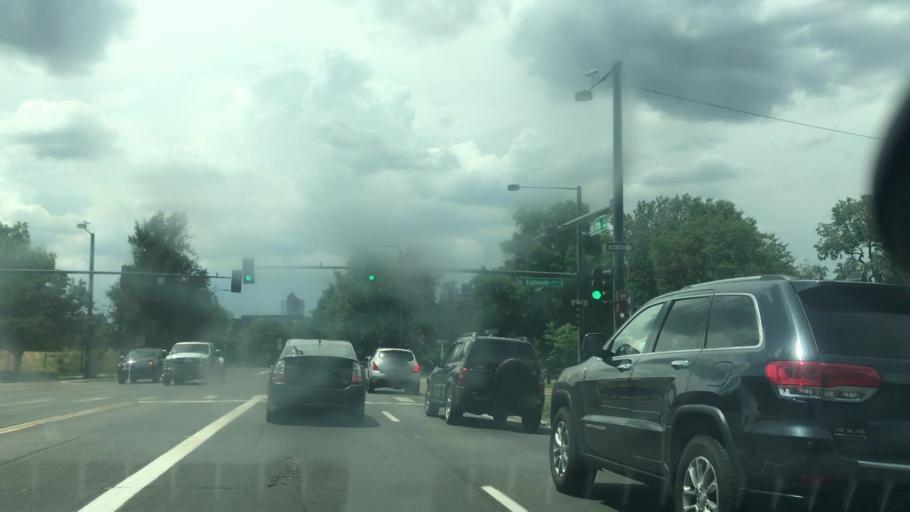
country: US
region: Colorado
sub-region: Denver County
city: Denver
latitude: 39.7439
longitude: -104.9563
